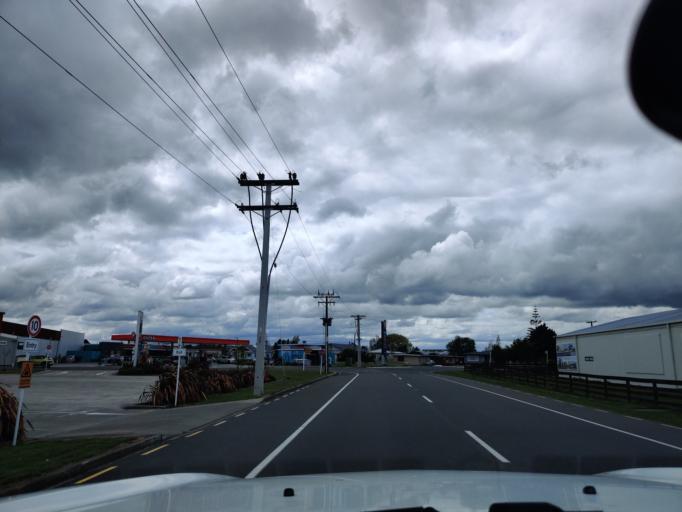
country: NZ
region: Manawatu-Wanganui
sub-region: Palmerston North City
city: Palmerston North
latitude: -40.2315
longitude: 175.5671
